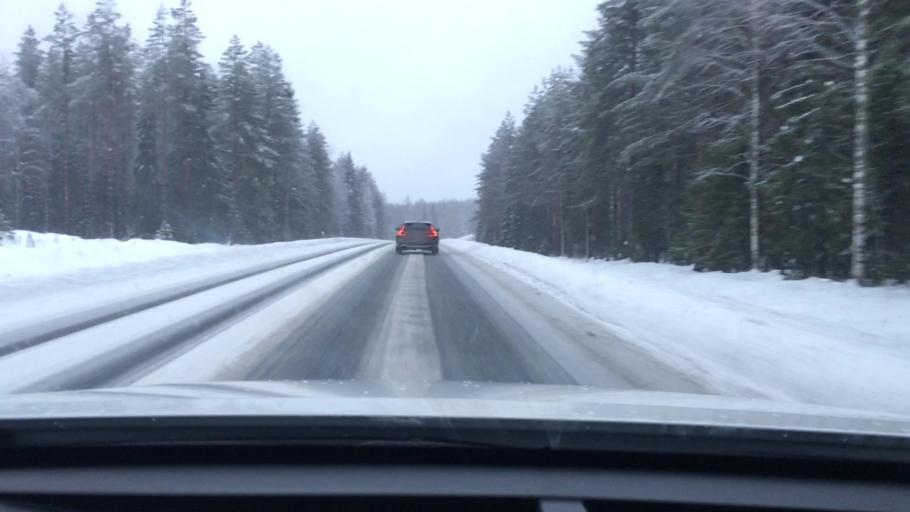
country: FI
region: Northern Savo
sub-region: Ylae-Savo
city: Sonkajaervi
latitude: 63.7721
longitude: 27.4150
